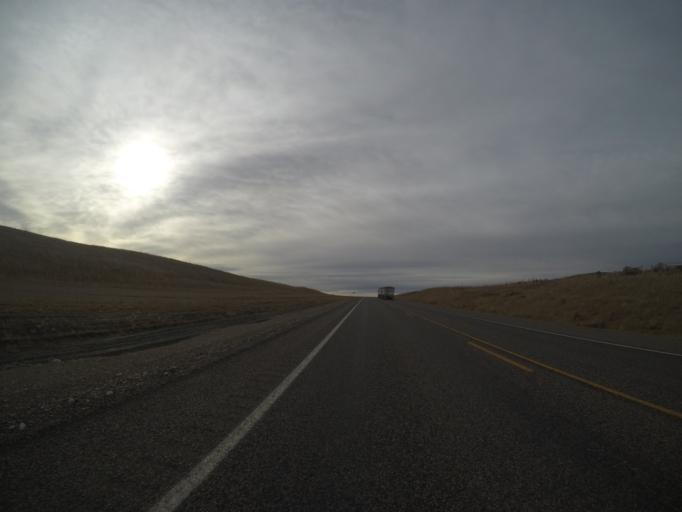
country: US
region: Montana
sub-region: Yellowstone County
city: Laurel
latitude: 45.5687
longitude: -108.8504
